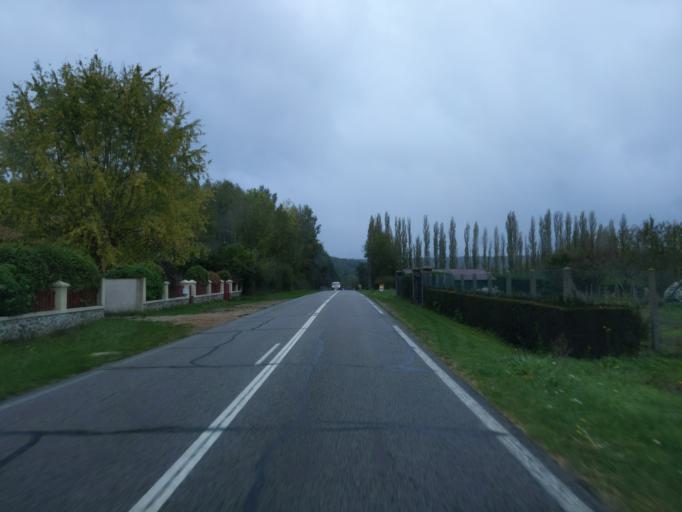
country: FR
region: Ile-de-France
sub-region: Departement des Yvelines
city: Dampierre-en-Yvelines
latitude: 48.6958
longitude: 1.9775
